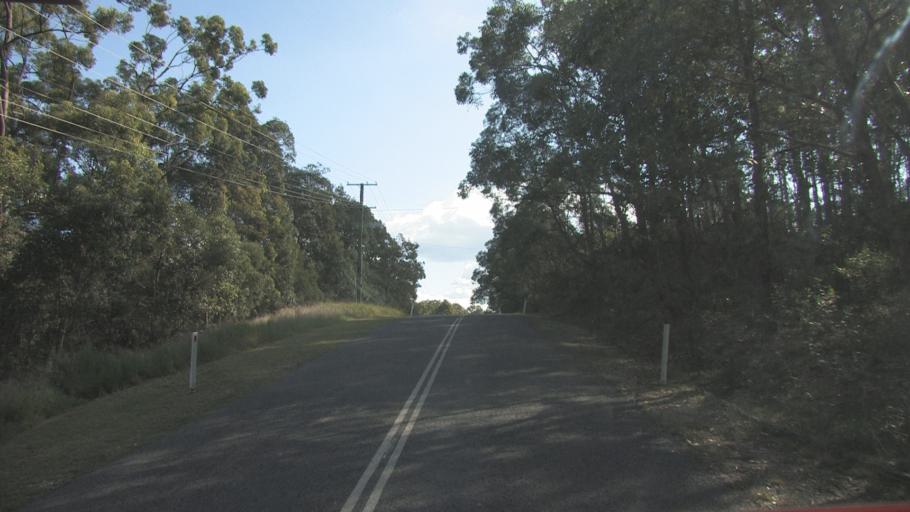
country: AU
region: Queensland
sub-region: Logan
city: Windaroo
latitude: -27.7390
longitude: 153.1664
